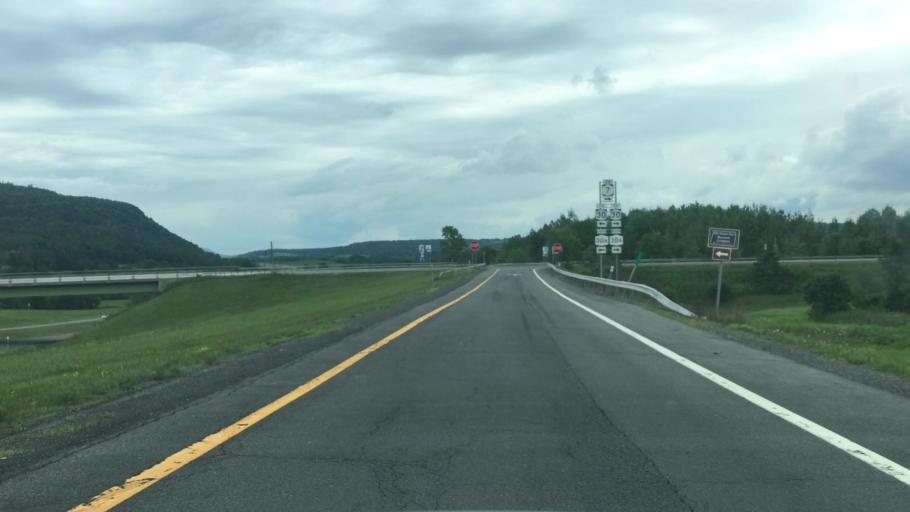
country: US
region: New York
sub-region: Schoharie County
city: Schoharie
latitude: 42.7079
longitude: -74.3124
